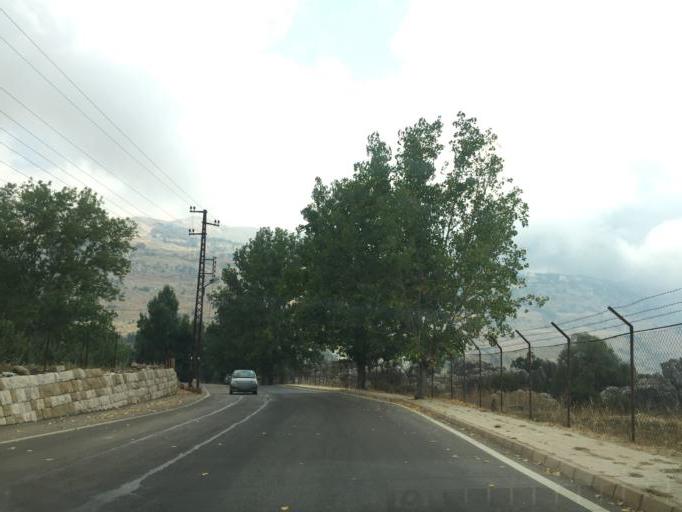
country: LB
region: Beqaa
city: Zahle
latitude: 34.0001
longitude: 35.8065
